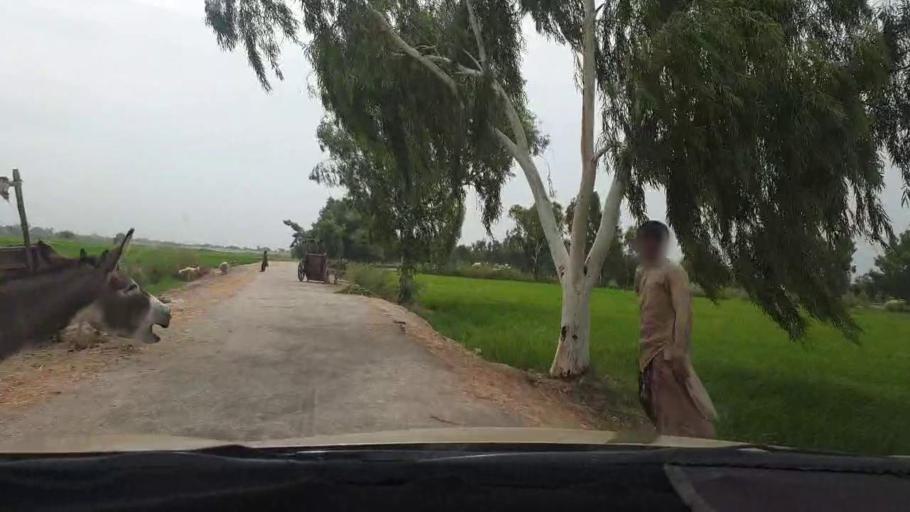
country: PK
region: Sindh
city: Naudero
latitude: 27.6231
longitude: 68.3255
